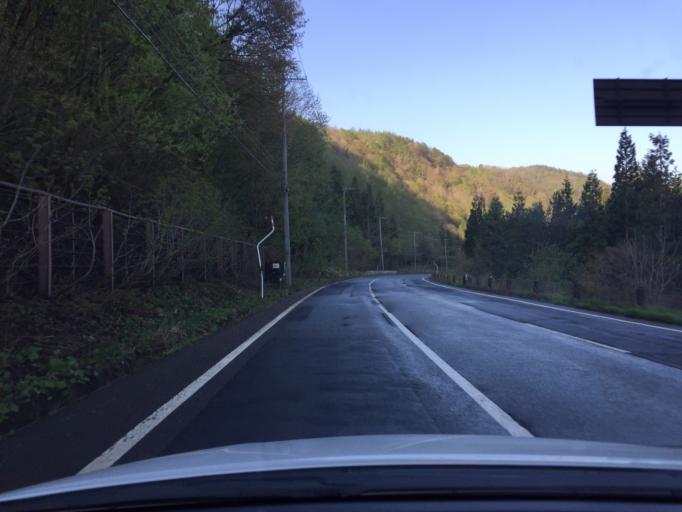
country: JP
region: Fukushima
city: Inawashiro
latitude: 37.6625
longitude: 140.0282
